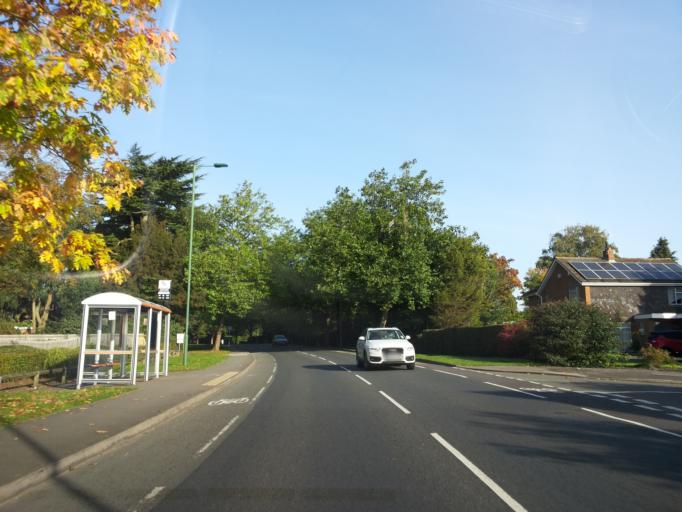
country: GB
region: England
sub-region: Solihull
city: Knowle
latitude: 52.3966
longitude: -1.7426
